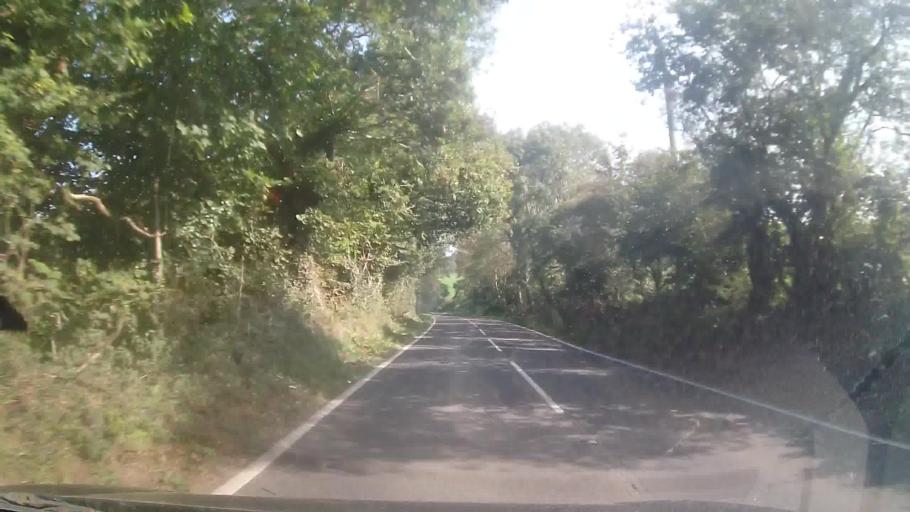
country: GB
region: Wales
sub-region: Pembrokeshire
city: Nevern
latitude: 52.0171
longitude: -4.7899
